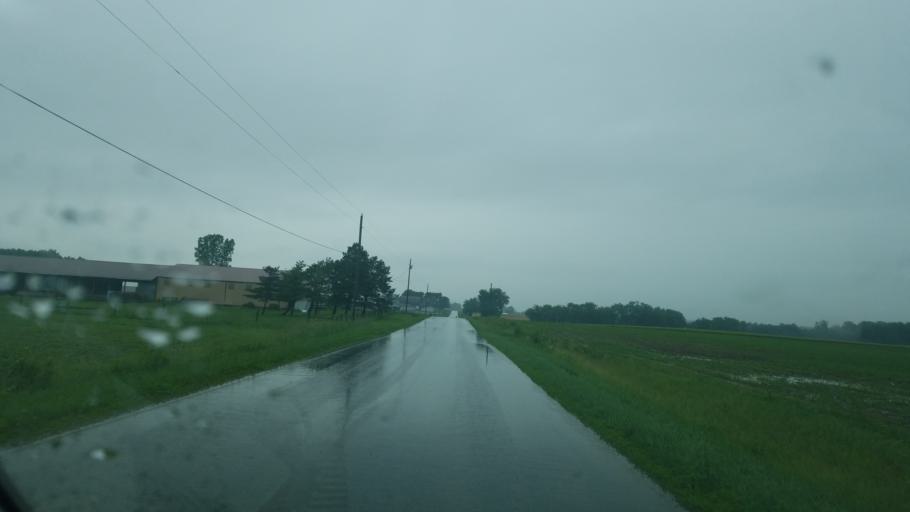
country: US
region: Ohio
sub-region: Huron County
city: Greenwich
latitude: 40.9972
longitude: -82.5825
